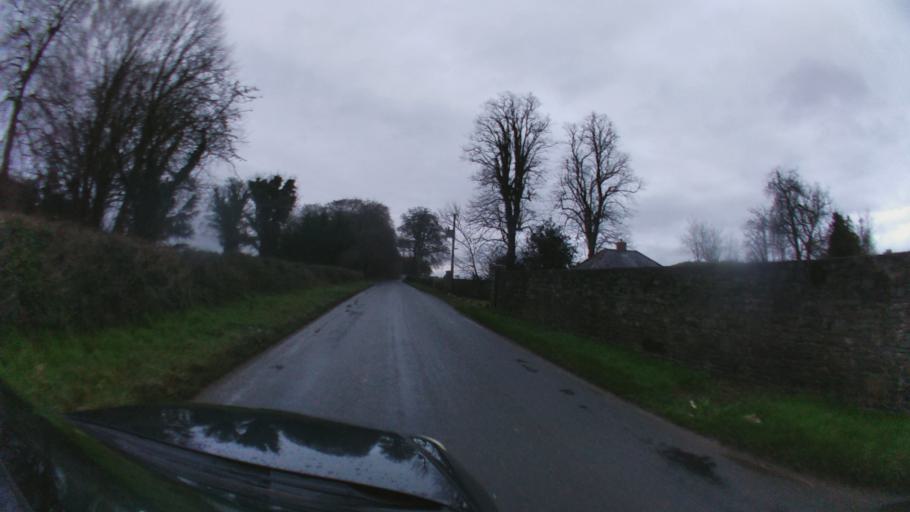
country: IE
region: Leinster
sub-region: County Carlow
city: Bagenalstown
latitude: 52.6657
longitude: -6.9900
